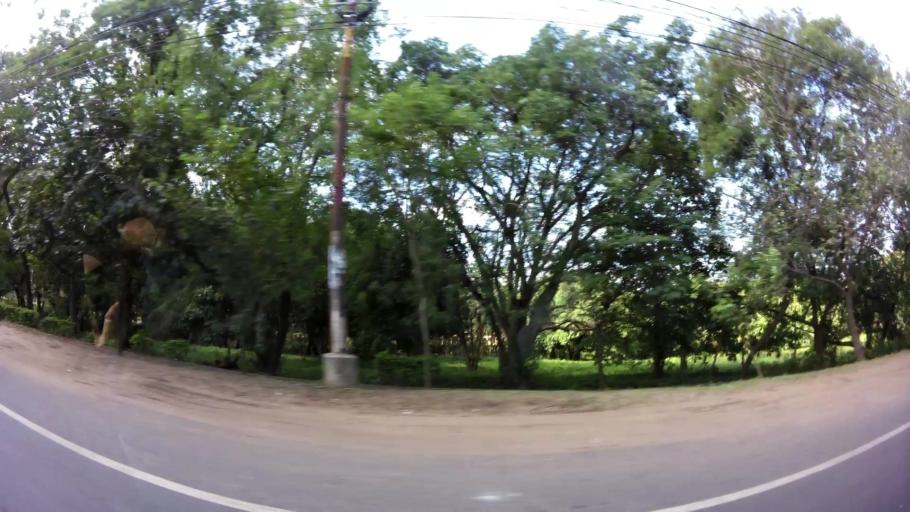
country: PY
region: Central
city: Fernando de la Mora
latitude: -25.3414
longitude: -57.5165
